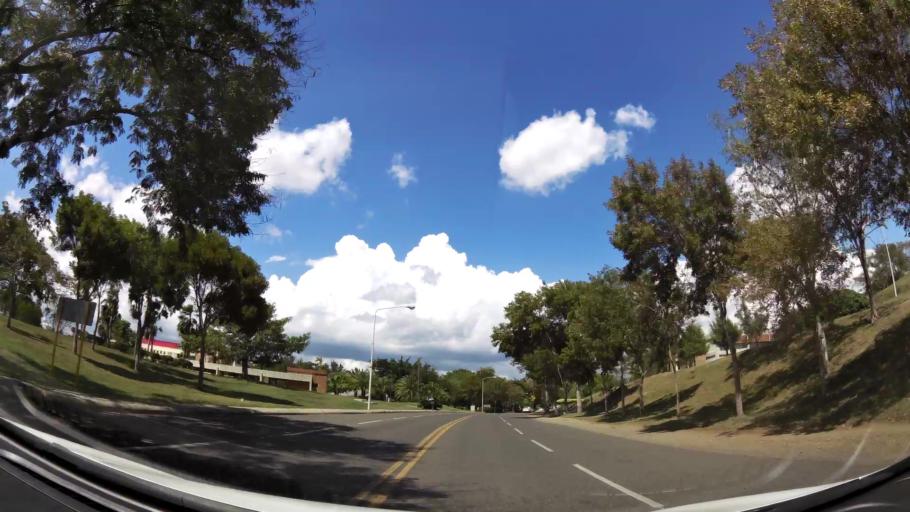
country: DO
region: Santiago
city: Santiago de los Caballeros
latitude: 19.4434
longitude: -70.6860
